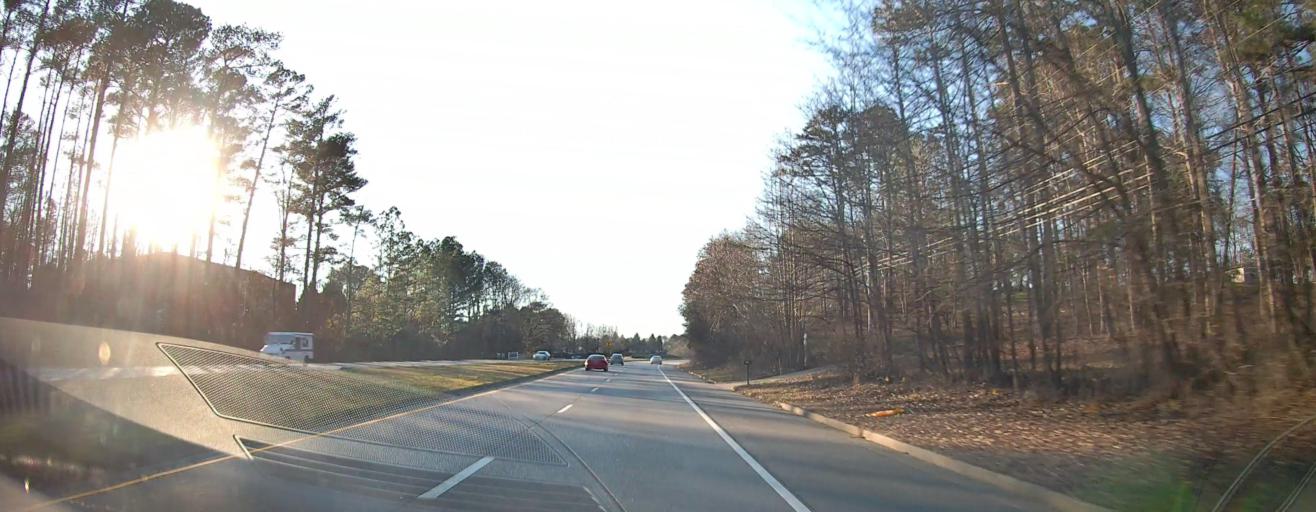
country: US
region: Georgia
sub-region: Fayette County
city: Fayetteville
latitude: 33.4486
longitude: -84.4986
